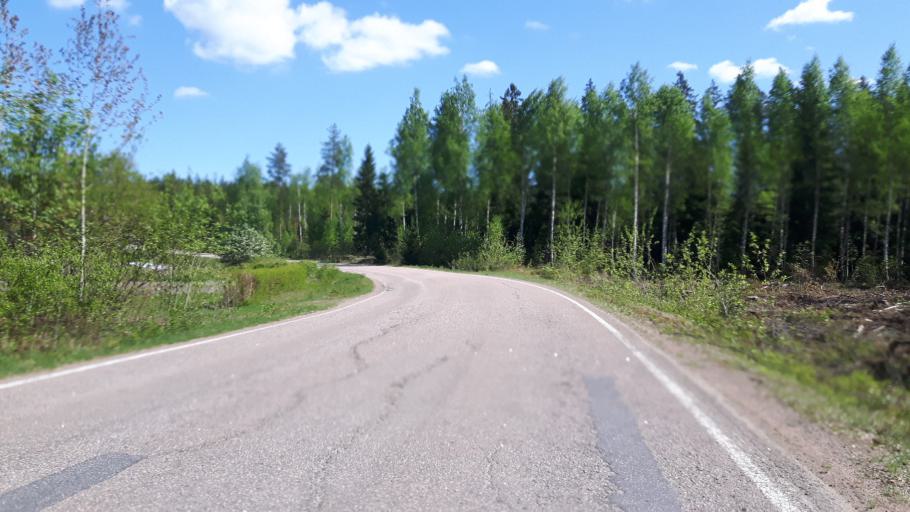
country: FI
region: Kymenlaakso
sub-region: Kotka-Hamina
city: Virolahti
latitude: 60.5514
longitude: 27.6774
